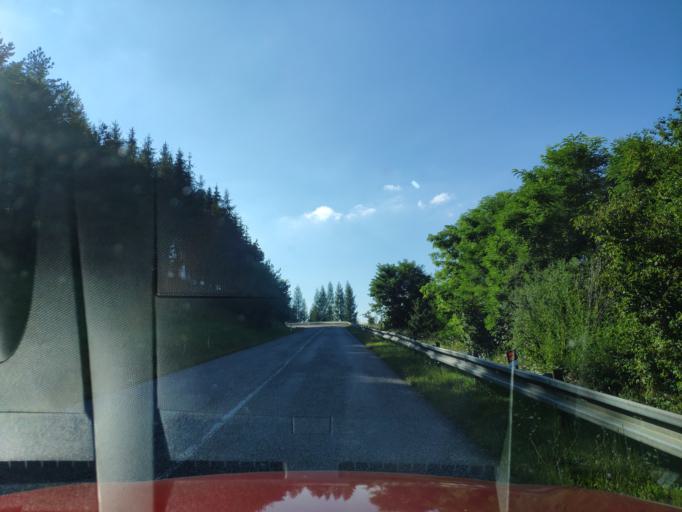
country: SK
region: Presovsky
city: Snina
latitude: 49.0519
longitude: 22.3001
